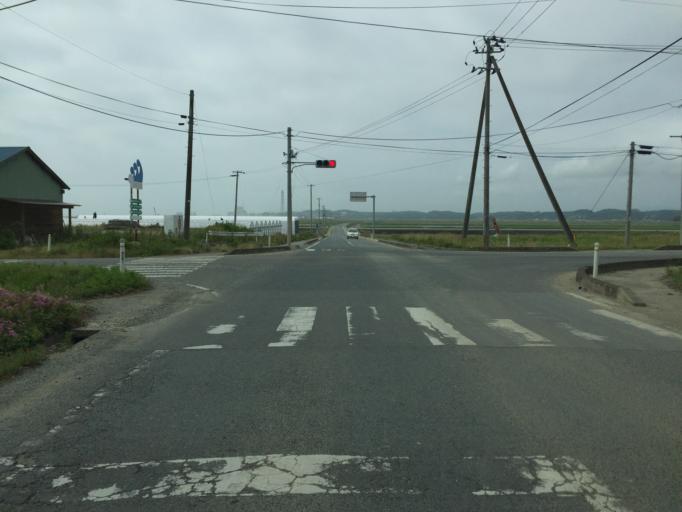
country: JP
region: Fukushima
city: Namie
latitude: 37.7071
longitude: 141.0053
